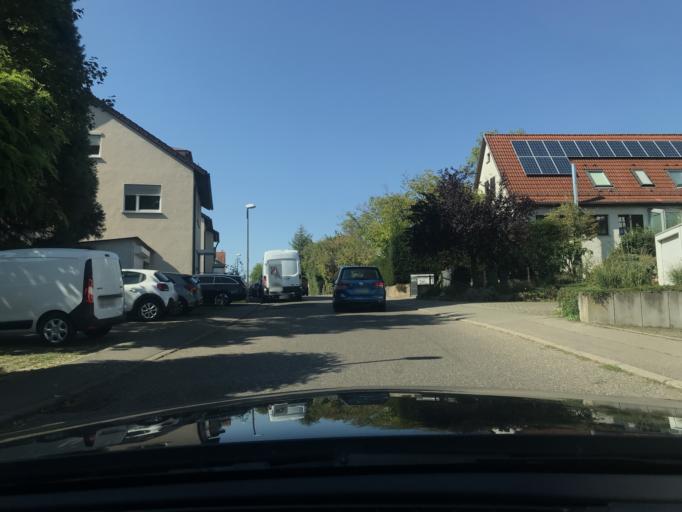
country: DE
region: Baden-Wuerttemberg
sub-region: Regierungsbezirk Stuttgart
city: Ostfildern
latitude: 48.7346
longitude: 9.2129
